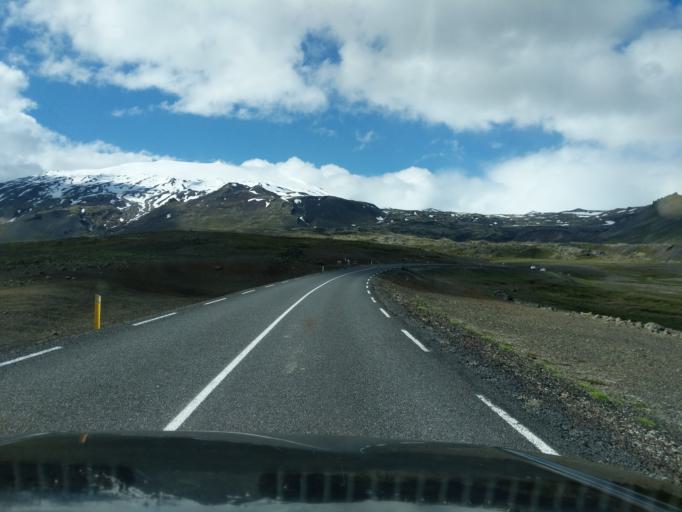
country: IS
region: West
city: Olafsvik
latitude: 64.7552
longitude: -23.6697
